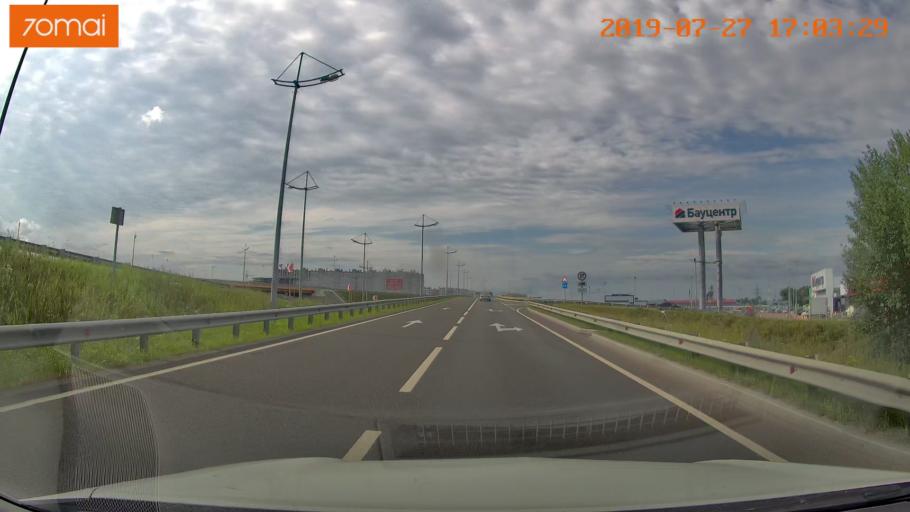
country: RU
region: Kaliningrad
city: Bol'shoe Isakovo
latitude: 54.7052
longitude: 20.6017
